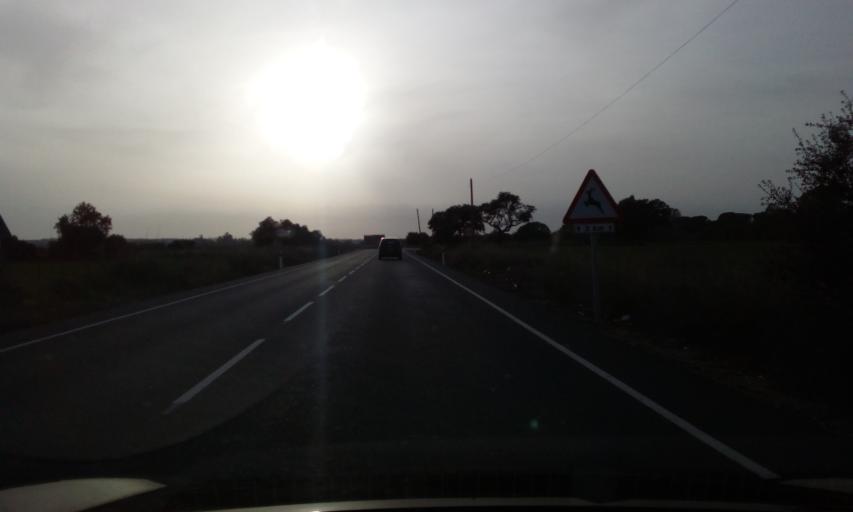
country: ES
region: Andalusia
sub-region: Provincia de Huelva
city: Lucena del Puerto
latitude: 37.3327
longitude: -6.7533
